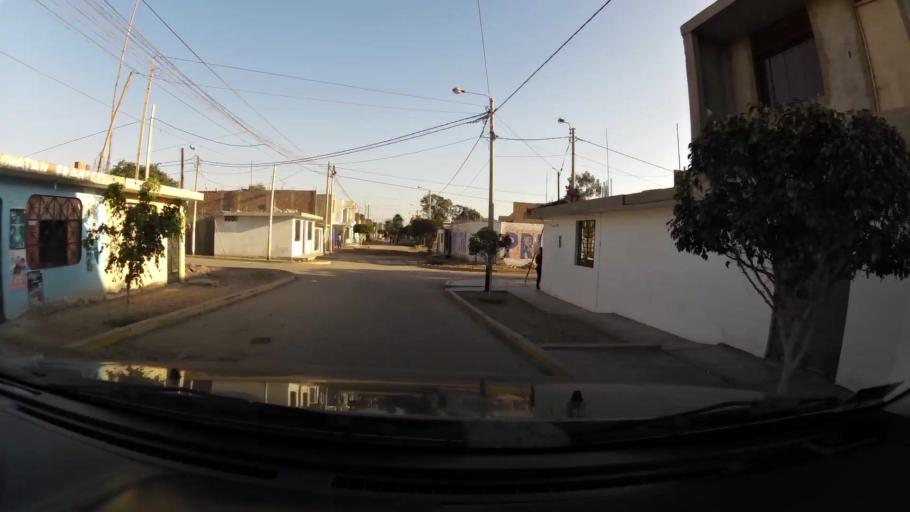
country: PE
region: Ica
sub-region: Provincia de Pisco
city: Villa Tupac Amaru
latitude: -13.7170
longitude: -76.1520
